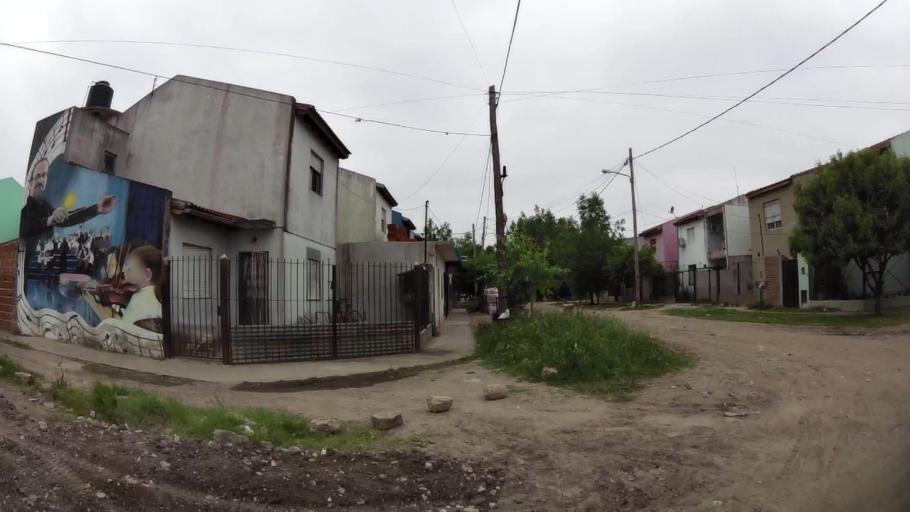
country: AR
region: Buenos Aires
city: San Justo
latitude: -34.6974
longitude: -58.5548
